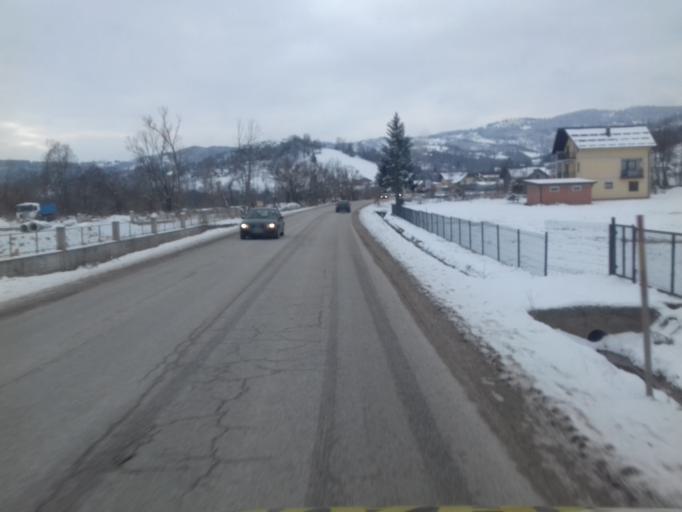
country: BA
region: Republika Srpska
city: Pale
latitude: 43.8725
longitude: 18.5849
